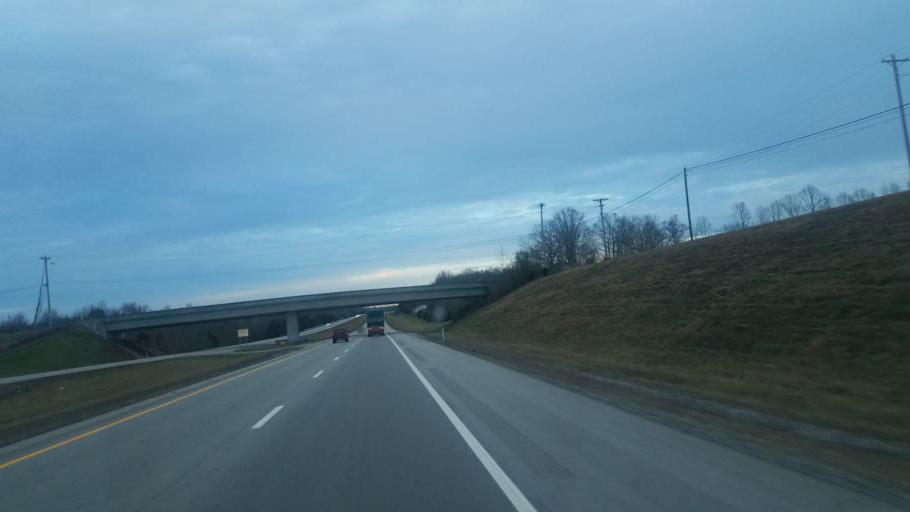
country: US
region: Tennessee
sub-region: Putnam County
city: Cookeville
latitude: 36.0867
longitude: -85.5058
